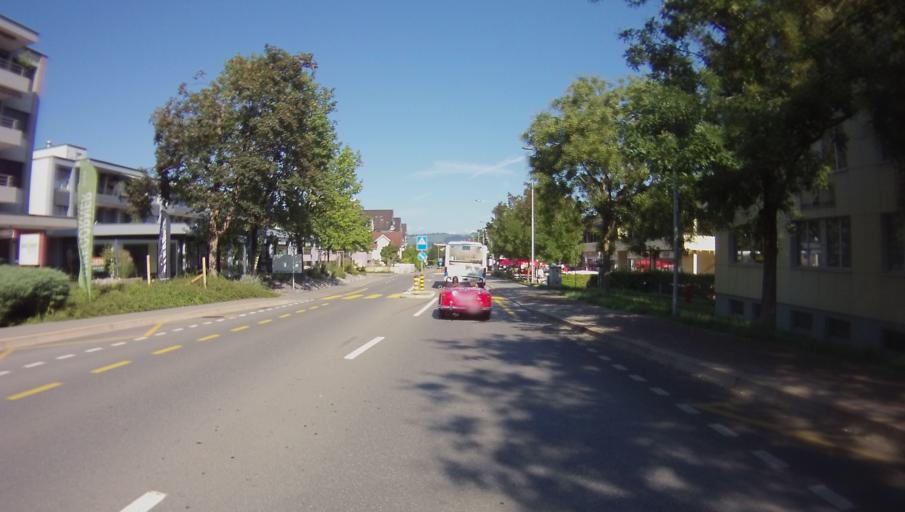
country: CH
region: Zug
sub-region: Zug
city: Cham
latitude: 47.1819
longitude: 8.4665
